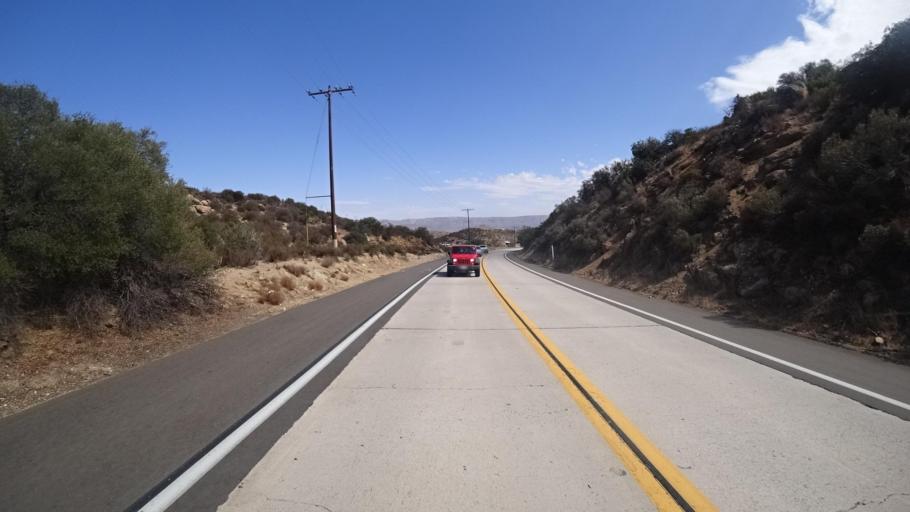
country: MX
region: Baja California
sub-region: Tecate
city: Cereso del Hongo
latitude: 32.6429
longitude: -116.2315
